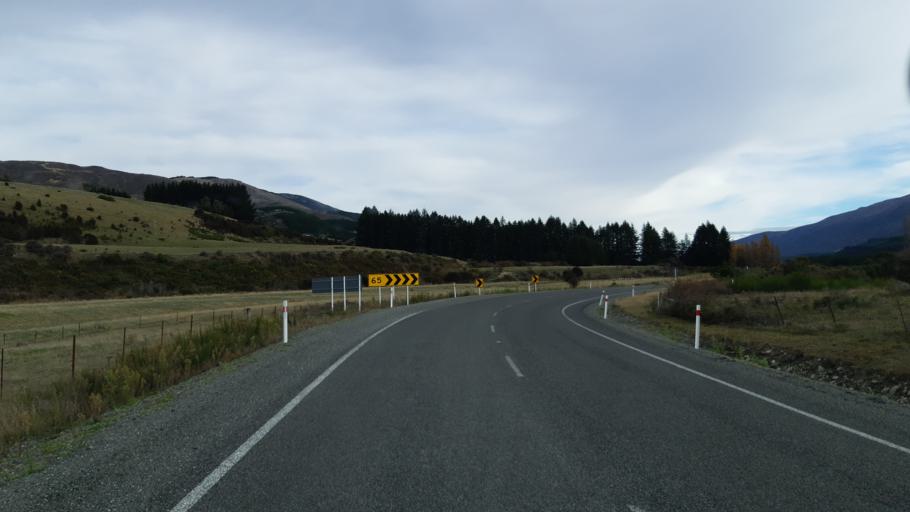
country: NZ
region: Tasman
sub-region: Tasman District
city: Brightwater
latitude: -41.6830
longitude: 173.1689
